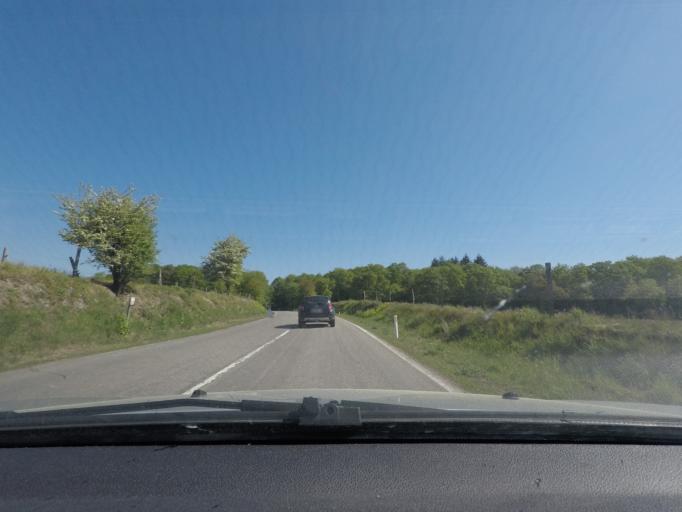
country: BE
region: Wallonia
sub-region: Province de Namur
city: Rochefort
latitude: 50.2080
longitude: 5.1455
